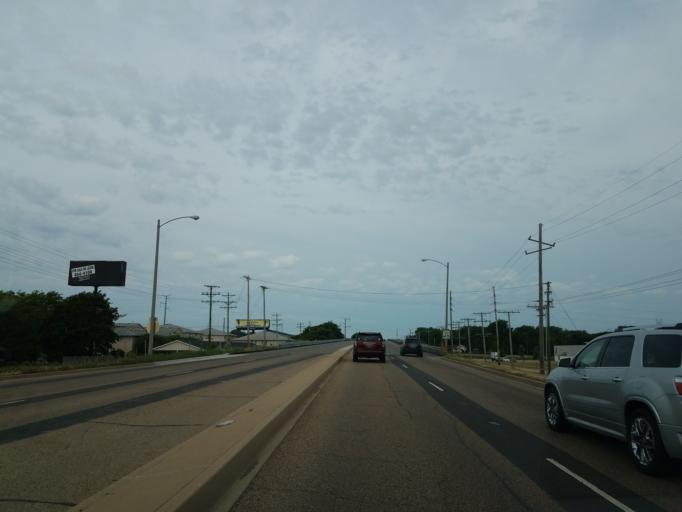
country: US
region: Illinois
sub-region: McLean County
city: Bloomington
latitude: 40.4596
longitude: -88.9774
